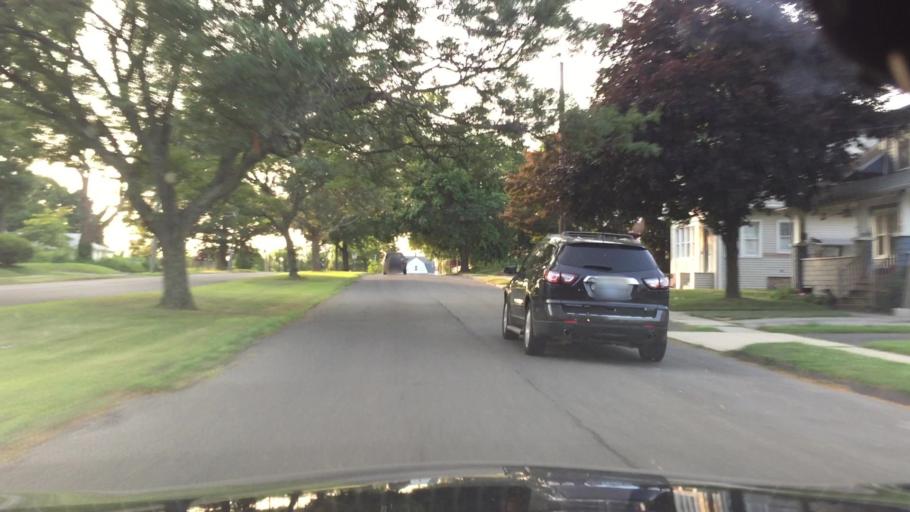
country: US
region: Connecticut
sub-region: Fairfield County
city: Stratford
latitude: 41.1983
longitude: -73.1075
